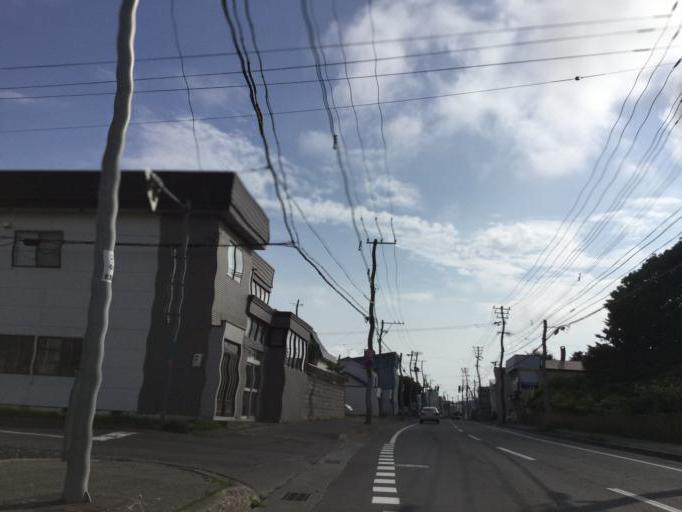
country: JP
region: Hokkaido
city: Wakkanai
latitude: 45.3930
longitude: 141.6833
